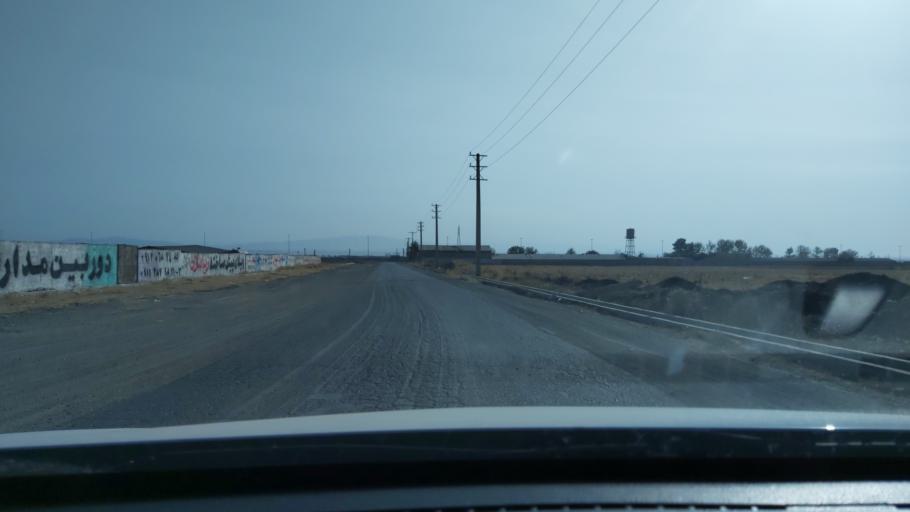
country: IR
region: Alborz
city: Hashtgerd
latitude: 35.9301
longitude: 50.7759
